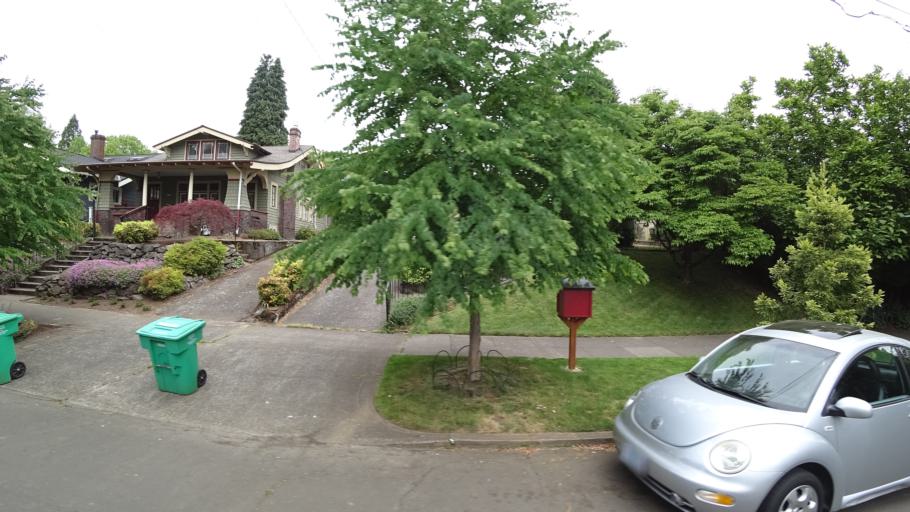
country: US
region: Oregon
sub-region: Multnomah County
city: Portland
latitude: 45.5249
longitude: -122.6178
